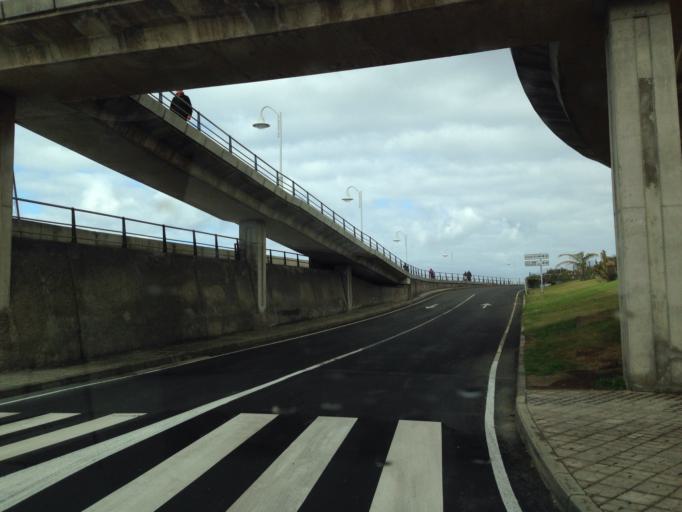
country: ES
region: Canary Islands
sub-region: Provincia de Las Palmas
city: Agaete
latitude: 28.1024
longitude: -15.7127
